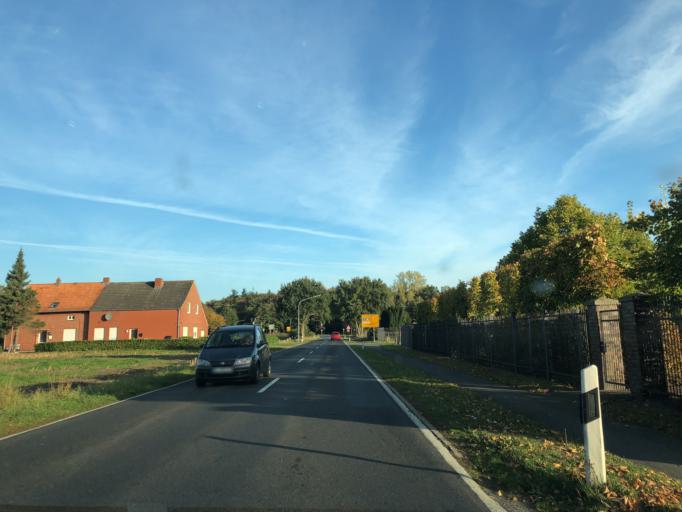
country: DE
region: Lower Saxony
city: Lehe
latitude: 53.0473
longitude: 7.3454
